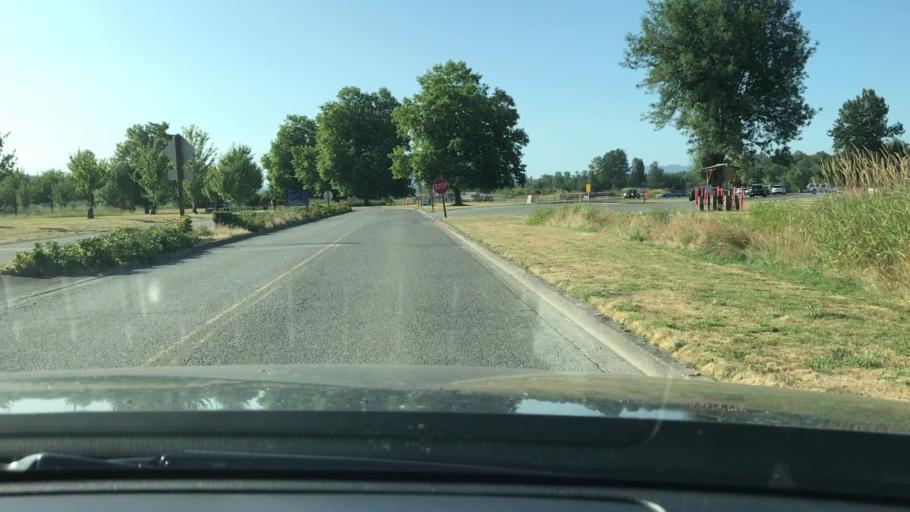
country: US
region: Washington
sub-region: King County
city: Redmond
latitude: 47.6622
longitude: -122.1113
